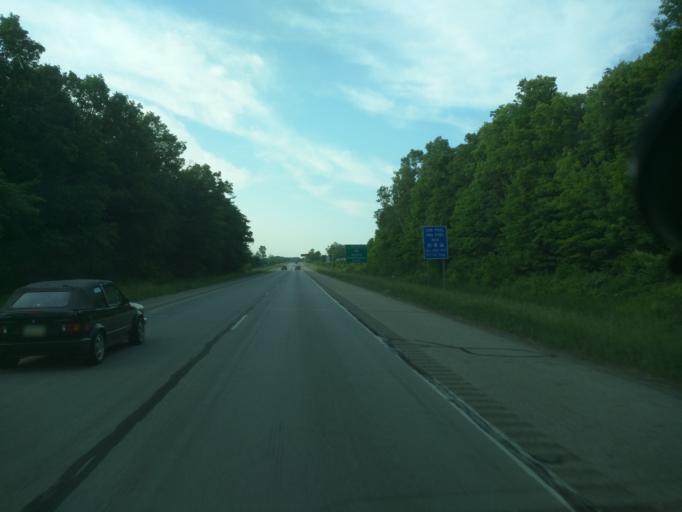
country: US
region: Michigan
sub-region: Ingham County
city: Holt
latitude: 42.6493
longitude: -84.4767
